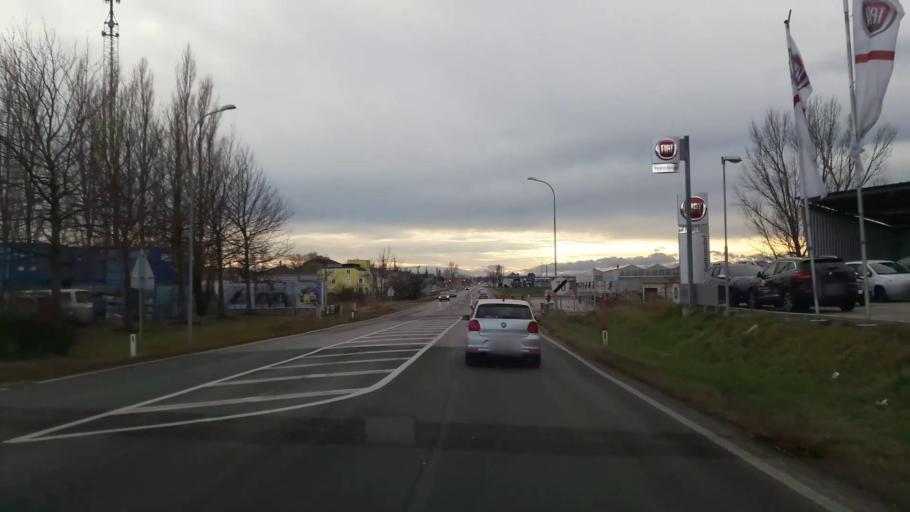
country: AT
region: Lower Austria
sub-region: Politischer Bezirk Modling
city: Guntramsdorf
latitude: 48.0429
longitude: 16.3051
